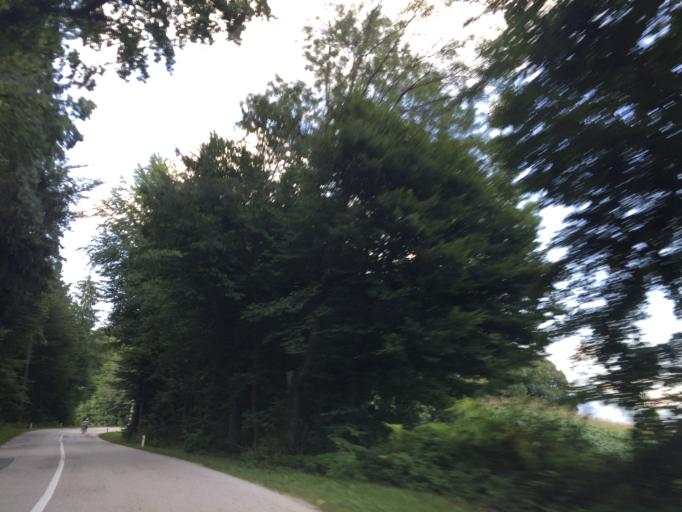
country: SI
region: Trzic
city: Bistrica pri Trzicu
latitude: 46.3052
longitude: 14.2675
